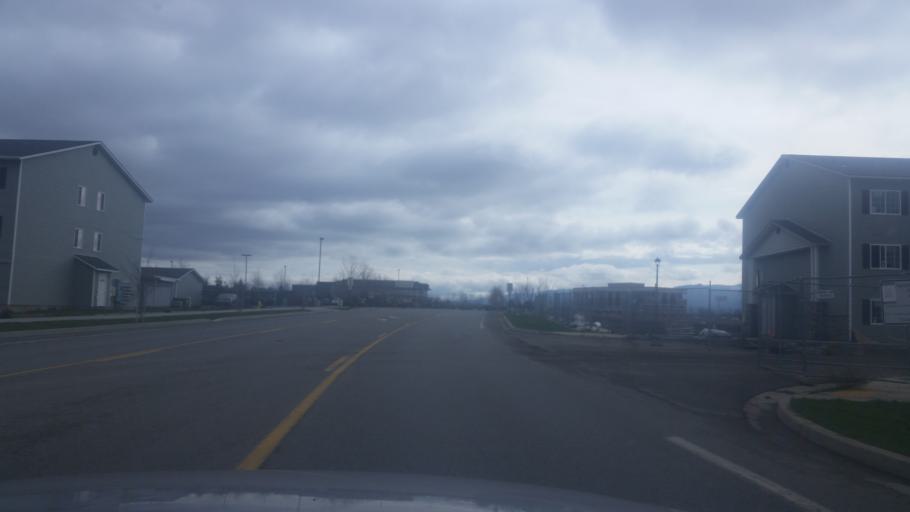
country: US
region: Washington
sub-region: Spokane County
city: Spokane Valley
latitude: 47.6775
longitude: -117.2301
